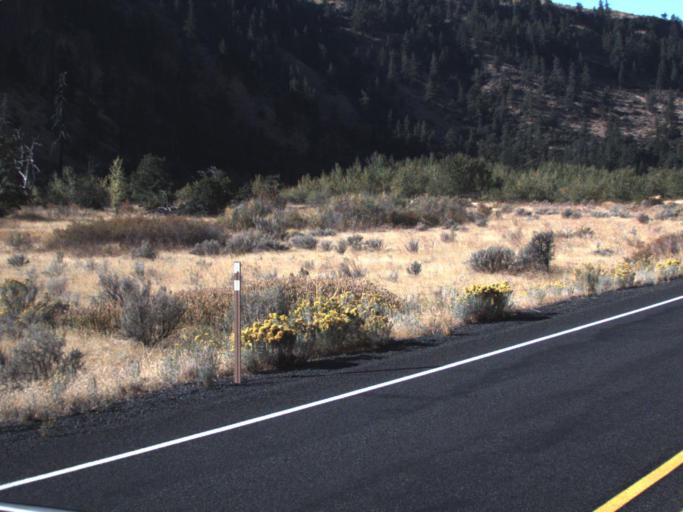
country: US
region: Washington
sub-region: Yakima County
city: Tieton
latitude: 46.7209
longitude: -120.8275
